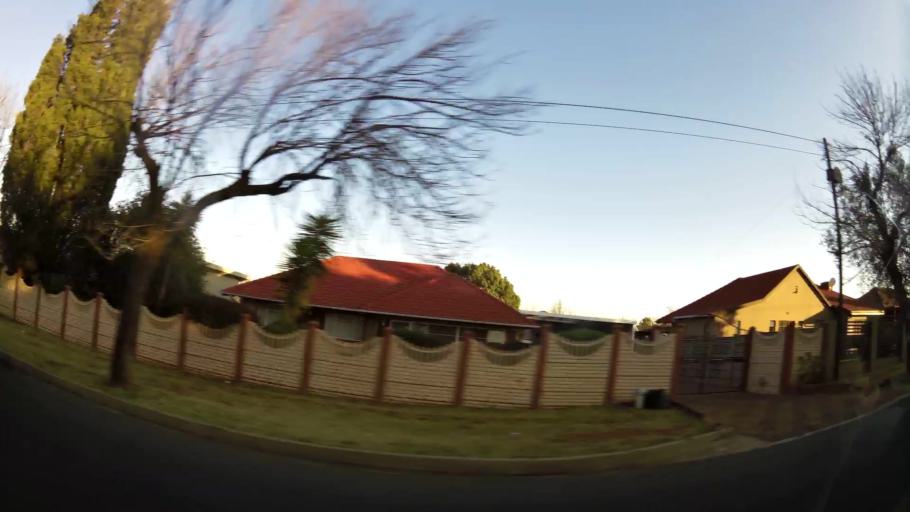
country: ZA
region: Gauteng
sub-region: City of Johannesburg Metropolitan Municipality
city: Roodepoort
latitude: -26.1564
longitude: 27.8827
